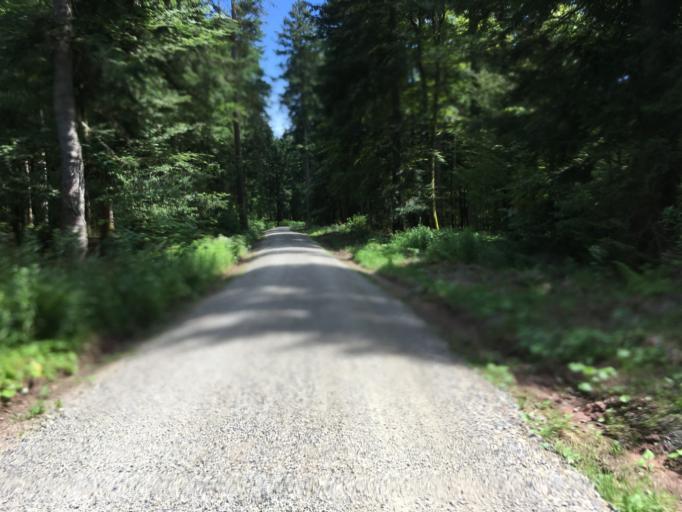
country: DE
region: Baden-Wuerttemberg
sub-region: Karlsruhe Region
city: Baiersbronn
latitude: 48.5327
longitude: 8.4250
